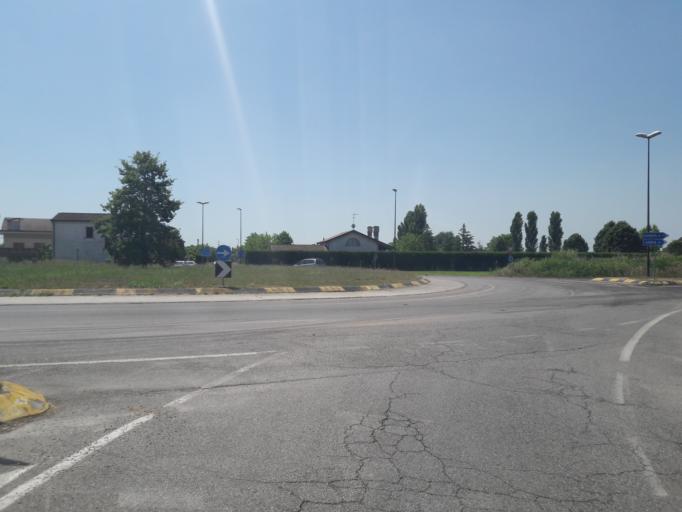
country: IT
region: Veneto
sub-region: Provincia di Rovigo
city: Taglio di Po
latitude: 44.9982
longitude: 12.2108
